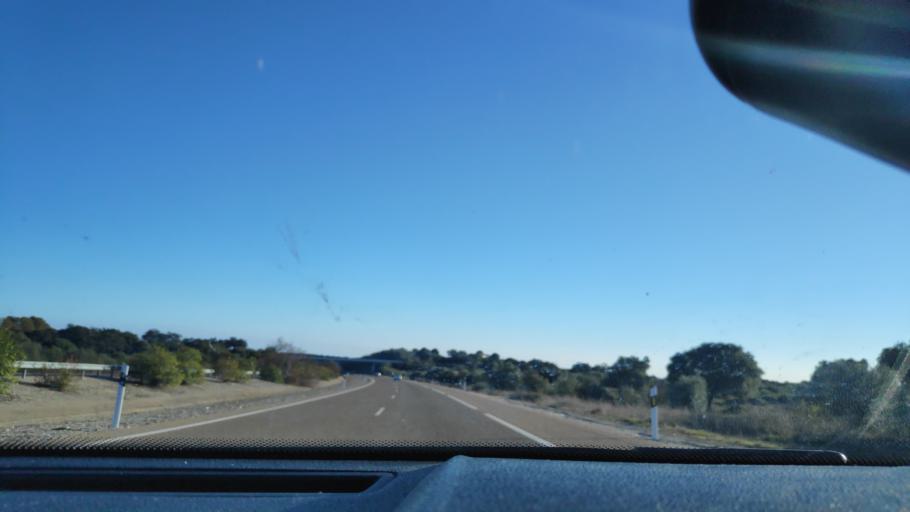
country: ES
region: Andalusia
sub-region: Provincia de Sevilla
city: Gerena
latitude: 37.5864
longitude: -6.1223
